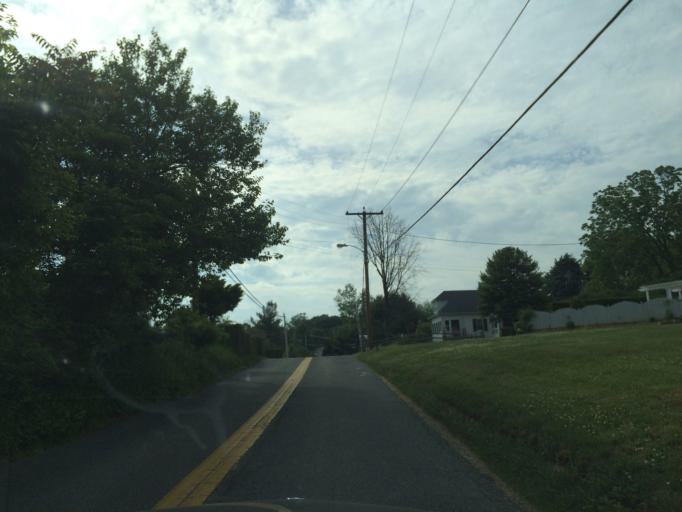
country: US
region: Maryland
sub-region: Baltimore County
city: Reisterstown
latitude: 39.4282
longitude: -76.8545
